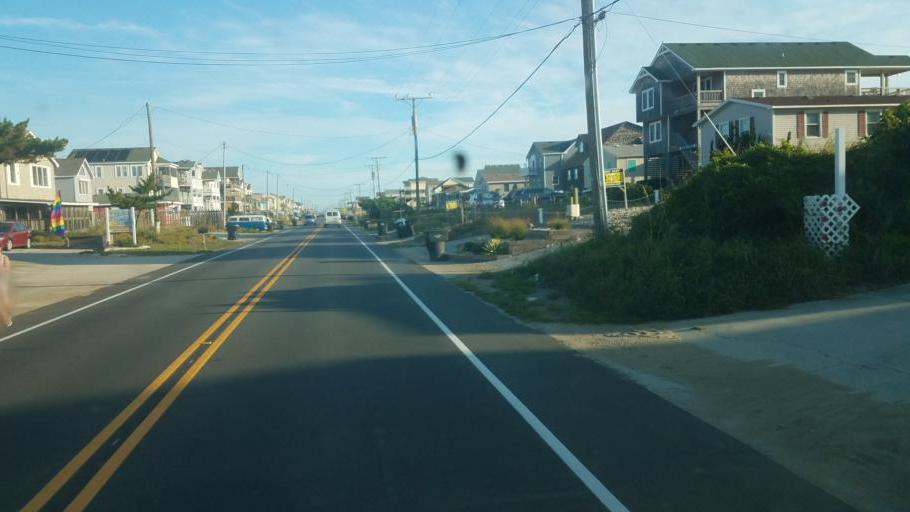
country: US
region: North Carolina
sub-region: Dare County
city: Kill Devil Hills
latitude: 36.0375
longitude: -75.6714
